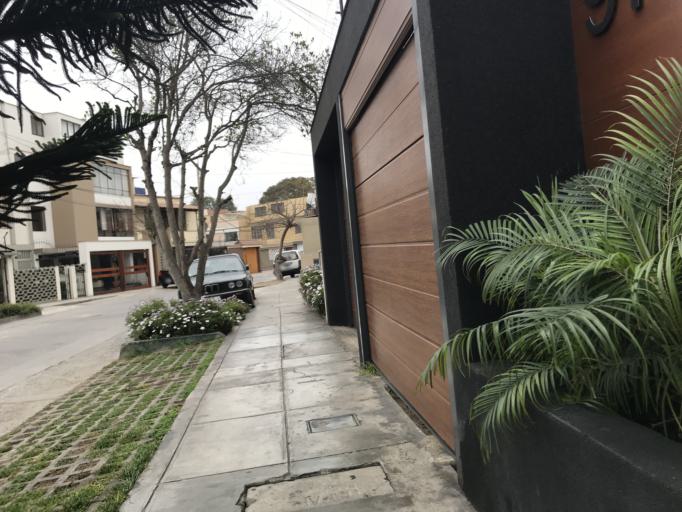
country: PE
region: Lima
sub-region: Lima
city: San Isidro
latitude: -12.0806
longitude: -77.0678
